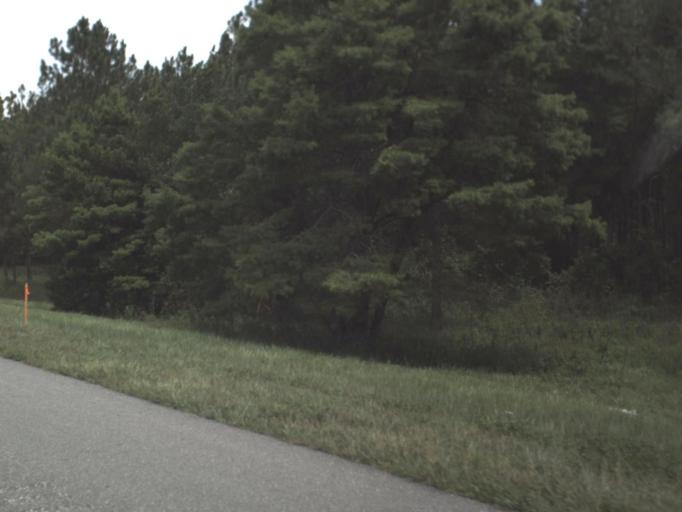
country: US
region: Florida
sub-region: Hernando County
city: Hill 'n Dale
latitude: 28.4945
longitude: -82.2484
